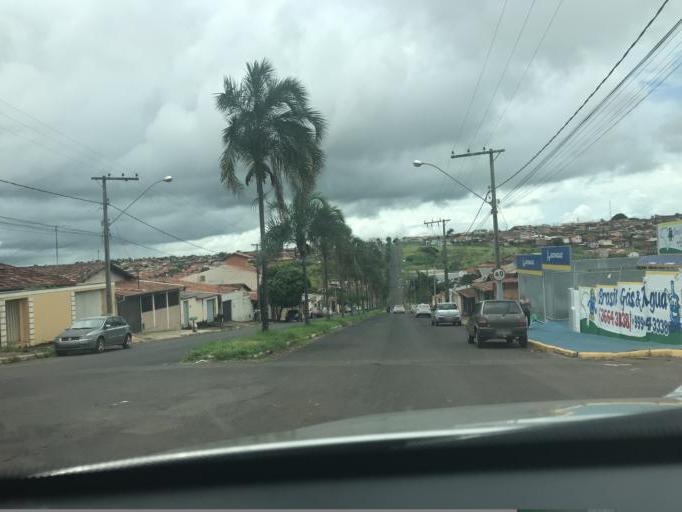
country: BR
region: Minas Gerais
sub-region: Araxa
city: Araxa
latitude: -19.5794
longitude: -46.9339
